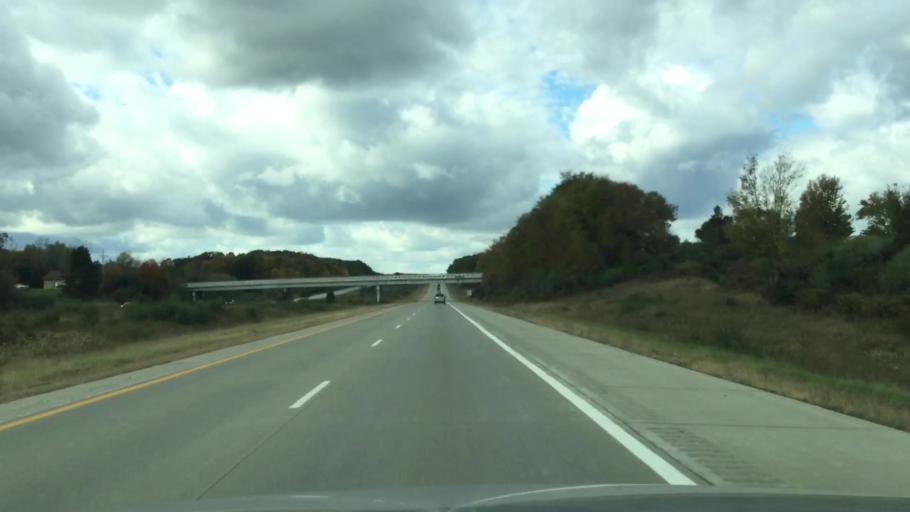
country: US
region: Michigan
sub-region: Lapeer County
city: Lapeer
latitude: 43.0228
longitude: -83.4069
